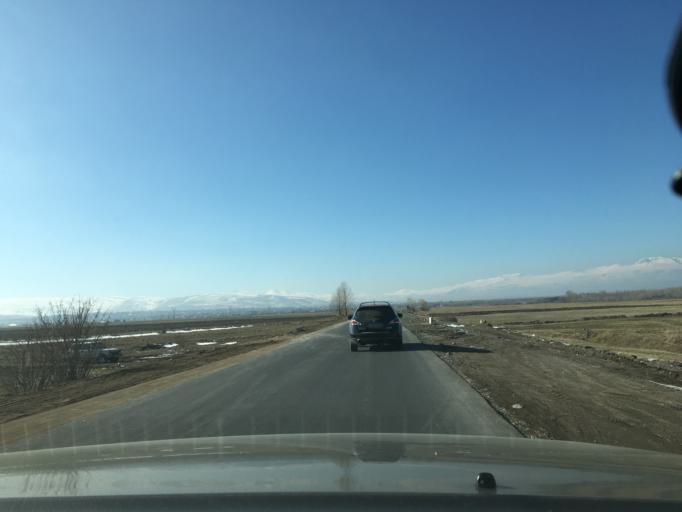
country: AM
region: Geghark'unik'i Marz
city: Vardenik
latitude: 40.1468
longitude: 45.4000
